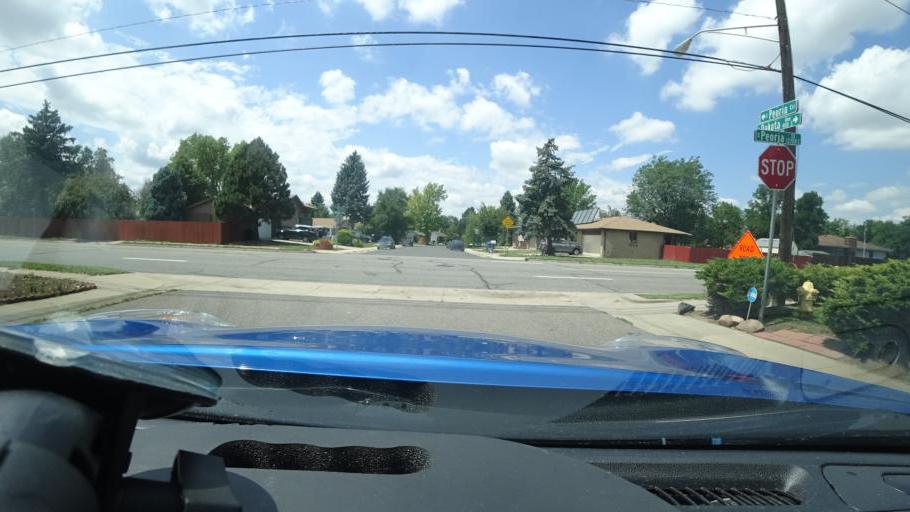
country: US
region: Colorado
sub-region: Adams County
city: Aurora
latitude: 39.7090
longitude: -104.8470
